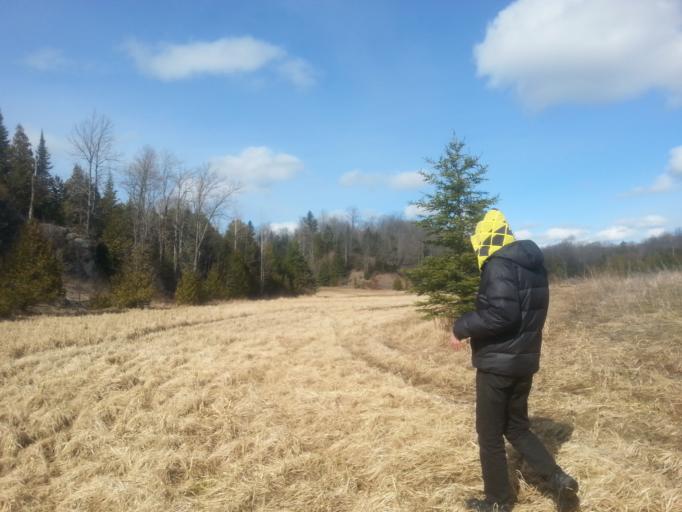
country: CA
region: Ontario
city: Omemee
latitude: 44.7444
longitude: -78.7763
